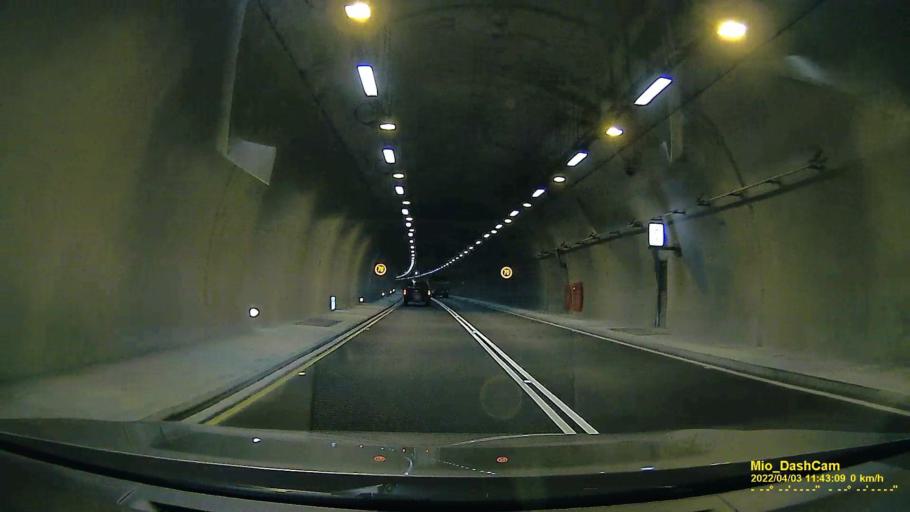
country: TW
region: Taiwan
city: Hengchun
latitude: 22.2634
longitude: 120.8356
